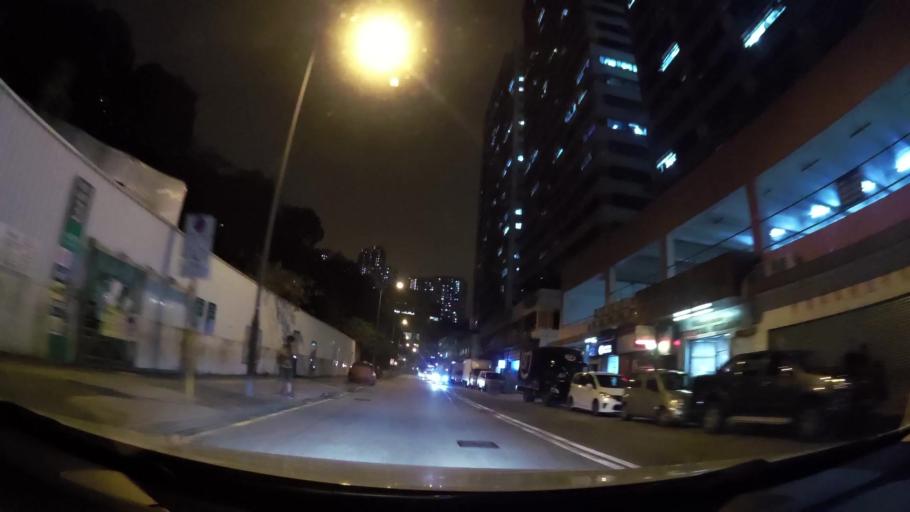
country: HK
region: Tsuen Wan
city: Tsuen Wan
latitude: 22.3586
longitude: 114.1321
